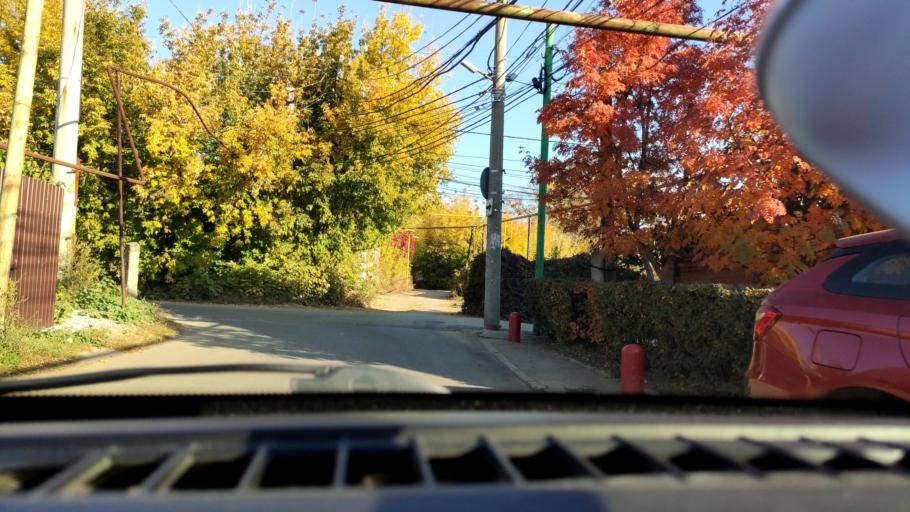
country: RU
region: Samara
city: Samara
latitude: 53.2662
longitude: 50.1929
